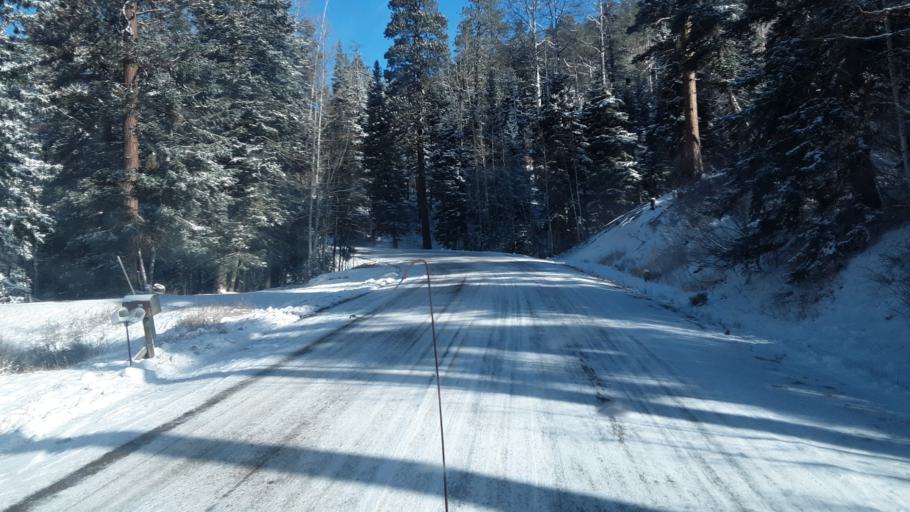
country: US
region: Colorado
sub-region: La Plata County
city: Bayfield
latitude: 37.3782
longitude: -107.6587
